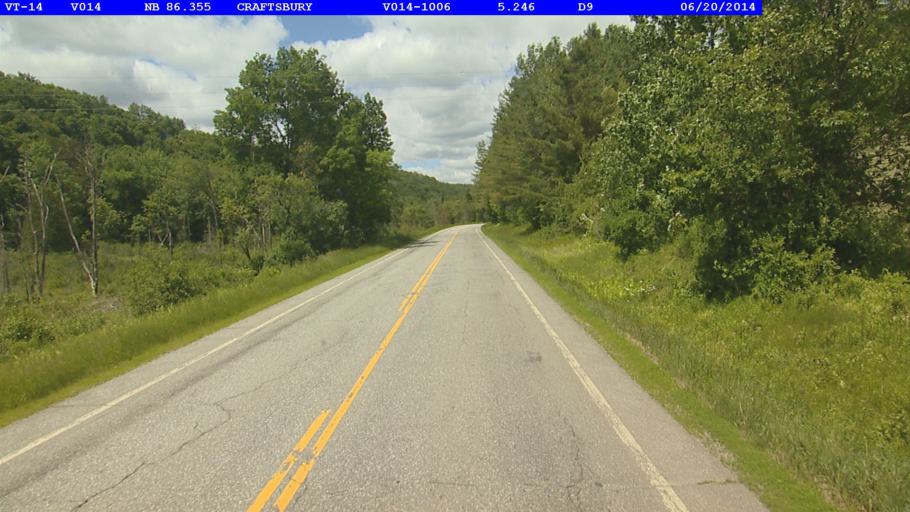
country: US
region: Vermont
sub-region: Caledonia County
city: Hardwick
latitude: 44.6661
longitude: -72.4039
